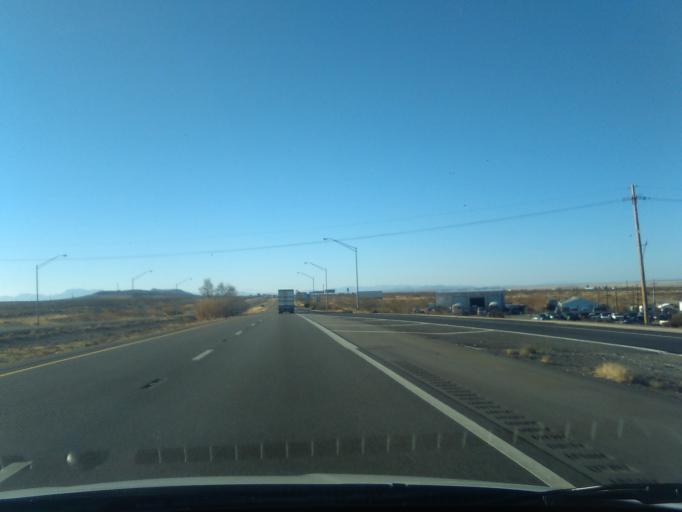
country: US
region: New Mexico
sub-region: Hidalgo County
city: Lordsburg
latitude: 32.3432
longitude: -108.7144
